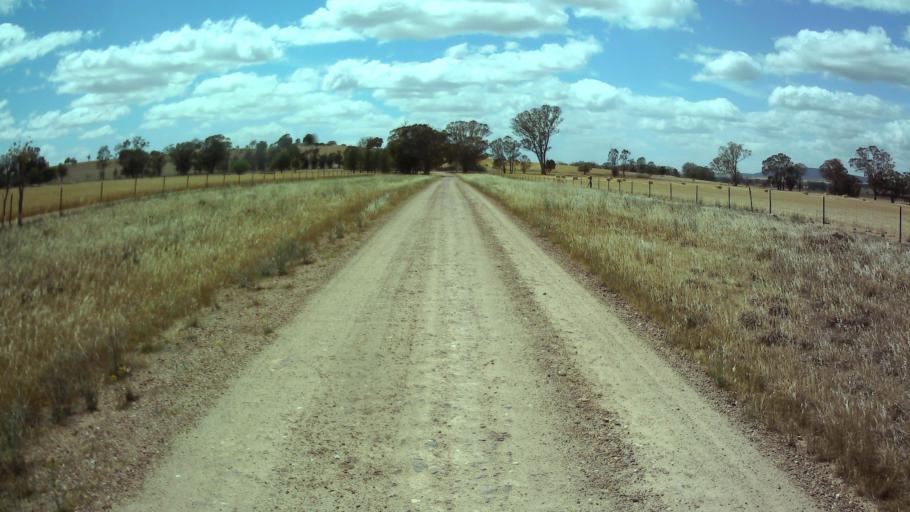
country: AU
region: New South Wales
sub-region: Weddin
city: Grenfell
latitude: -33.9915
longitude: 148.3360
